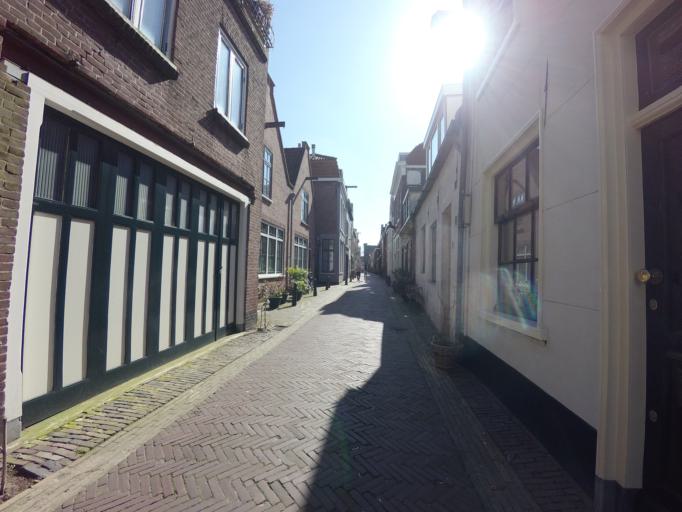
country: NL
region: North Holland
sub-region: Gemeente Haarlem
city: Haarlem
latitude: 52.3789
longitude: 4.6310
